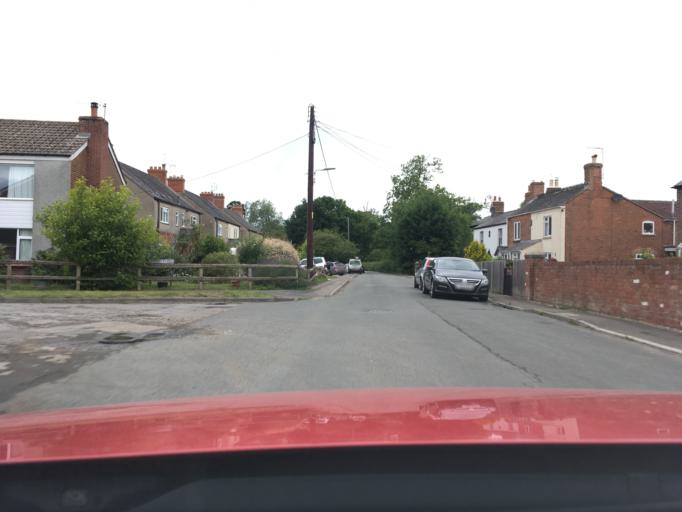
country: GB
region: England
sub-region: Gloucestershire
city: Stonehouse
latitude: 51.7845
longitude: -2.3674
